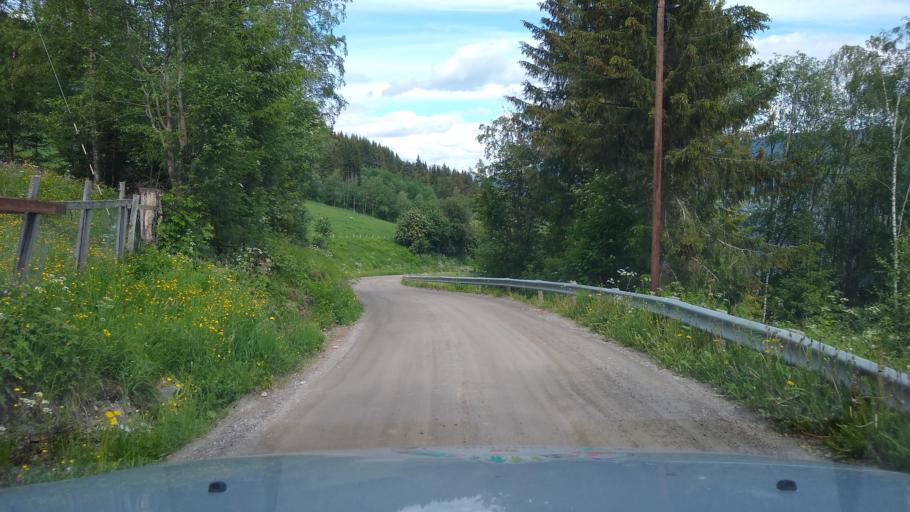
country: NO
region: Oppland
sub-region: Ringebu
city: Ringebu
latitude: 61.5109
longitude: 10.1351
